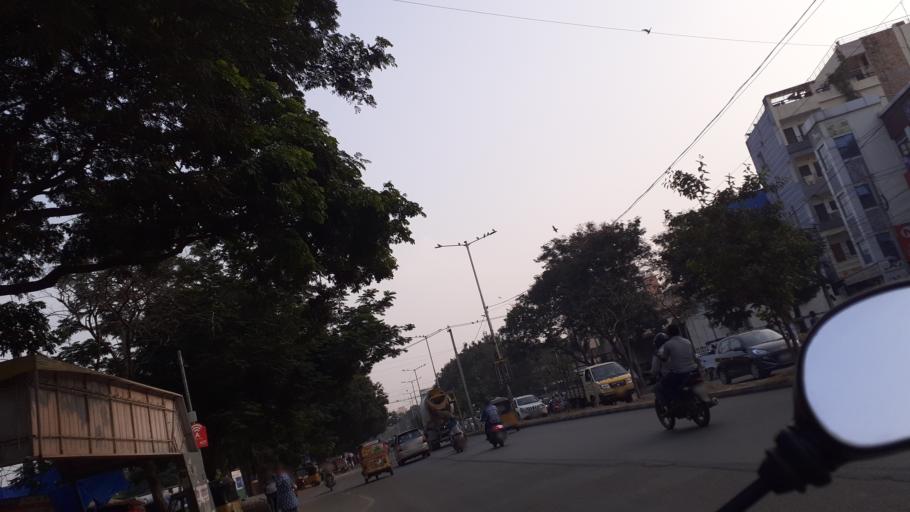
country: IN
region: Telangana
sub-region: Rangareddi
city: Kukatpalli
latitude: 17.4729
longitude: 78.3644
